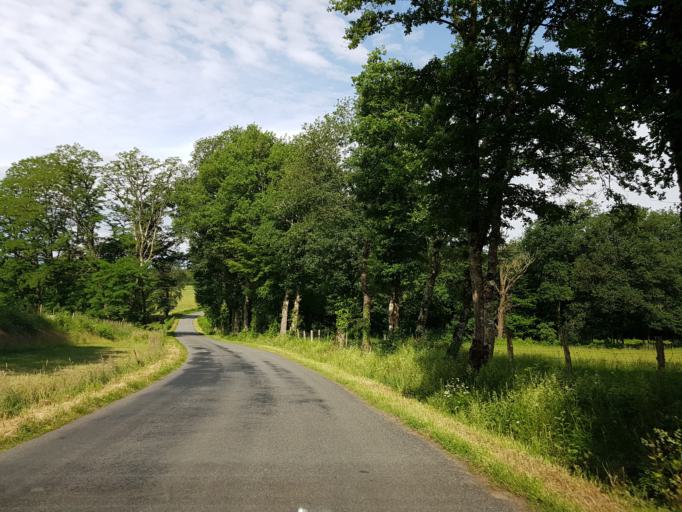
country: FR
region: Poitou-Charentes
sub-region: Departement de la Charente
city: Exideuil
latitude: 45.8996
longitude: 0.6822
